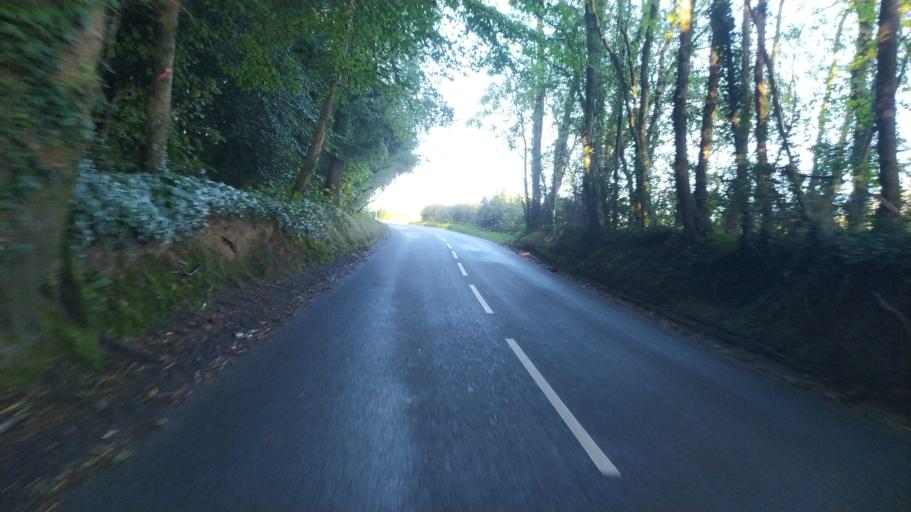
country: GB
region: England
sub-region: Dorset
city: Three Legged Cross
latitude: 50.8616
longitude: -1.9319
